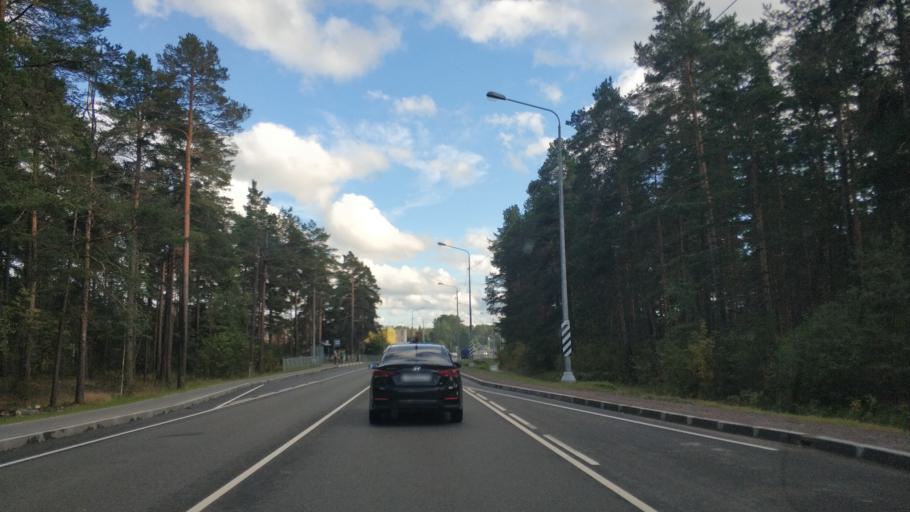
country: RU
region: Leningrad
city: Priozersk
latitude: 61.0041
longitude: 30.1802
